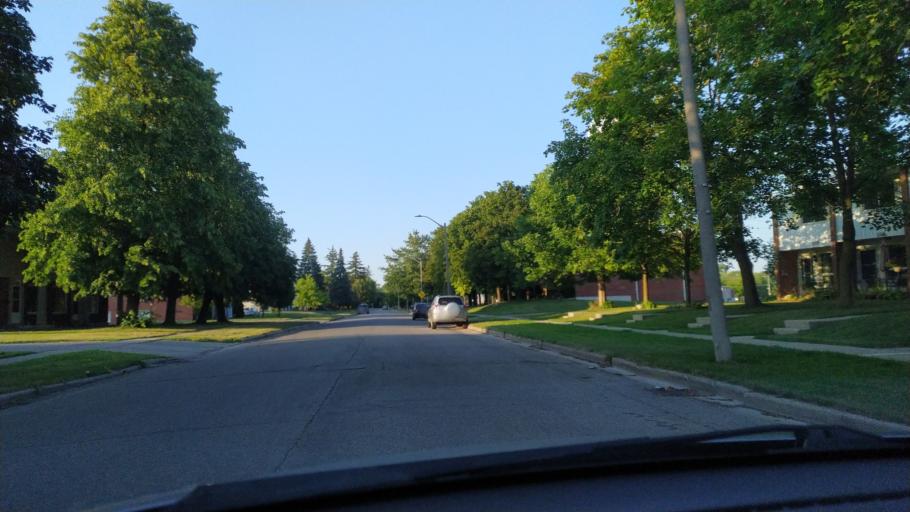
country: CA
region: Ontario
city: Stratford
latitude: 43.3566
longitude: -80.9893
